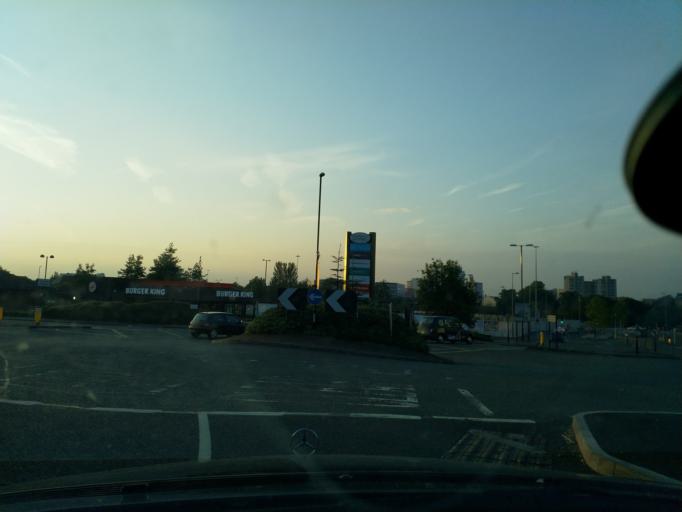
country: GB
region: England
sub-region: Coventry
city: Coventry
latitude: 52.4014
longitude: -1.5157
